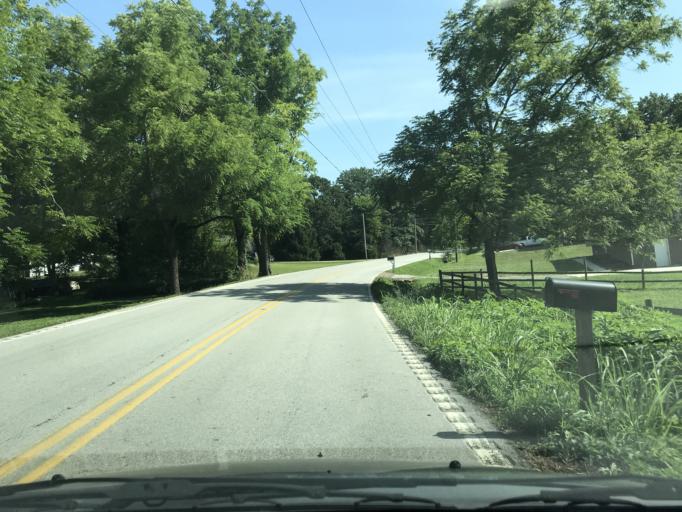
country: US
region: Tennessee
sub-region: Hamilton County
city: Lakesite
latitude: 35.2065
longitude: -85.0686
